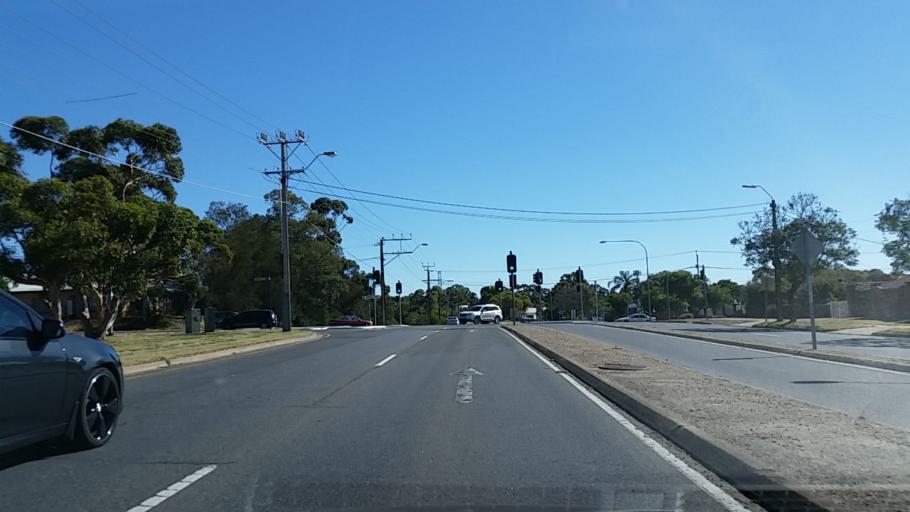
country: AU
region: South Australia
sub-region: Salisbury
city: Ingle Farm
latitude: -34.8341
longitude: 138.6270
